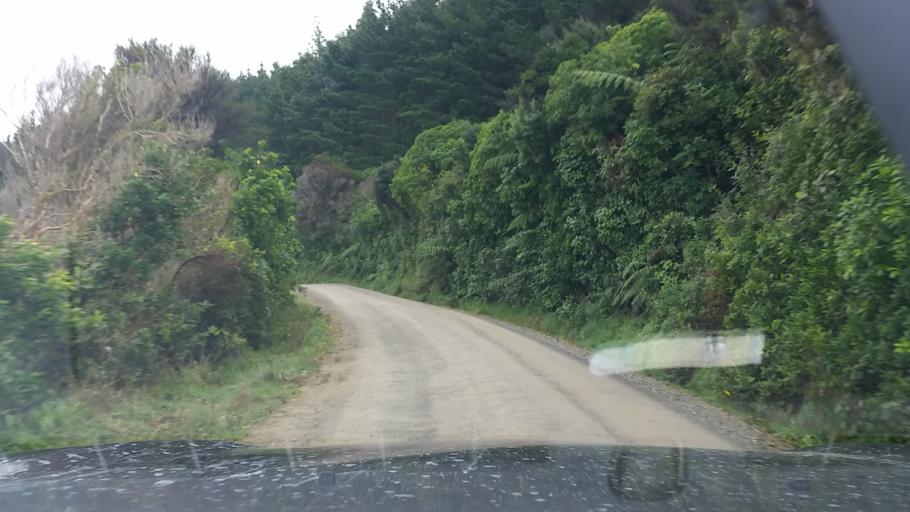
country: NZ
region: Marlborough
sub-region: Marlborough District
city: Picton
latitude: -41.1750
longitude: 174.0445
